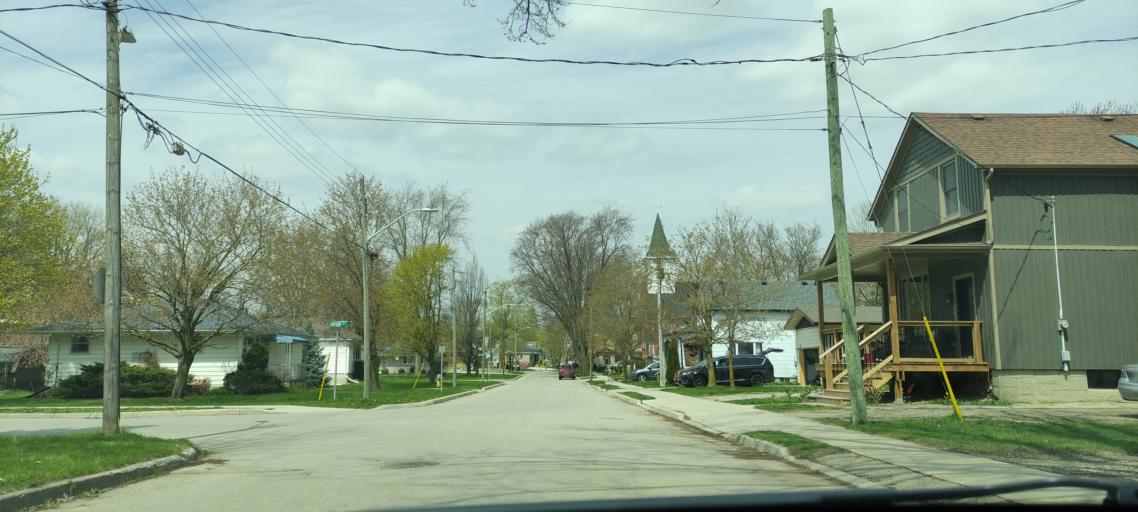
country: CA
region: Ontario
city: Stratford
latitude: 43.3210
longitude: -80.8312
